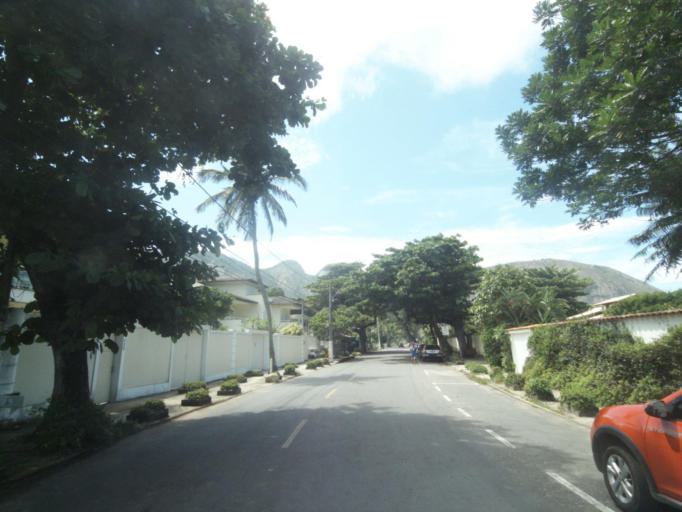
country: BR
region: Rio de Janeiro
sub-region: Niteroi
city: Niteroi
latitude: -22.9735
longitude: -43.0370
